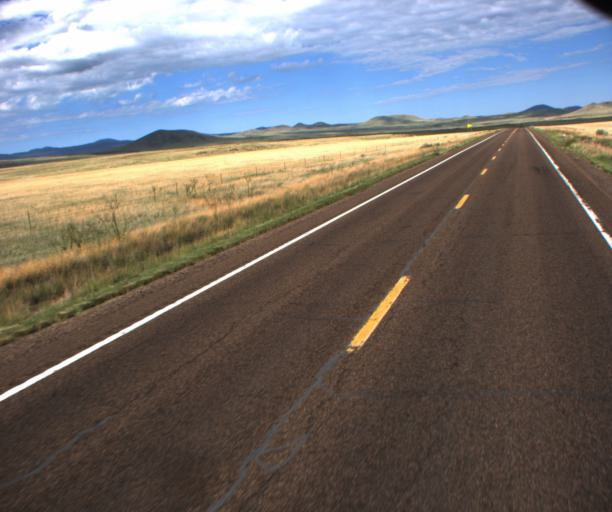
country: US
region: Arizona
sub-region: Apache County
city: Springerville
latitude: 34.1924
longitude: -109.3607
